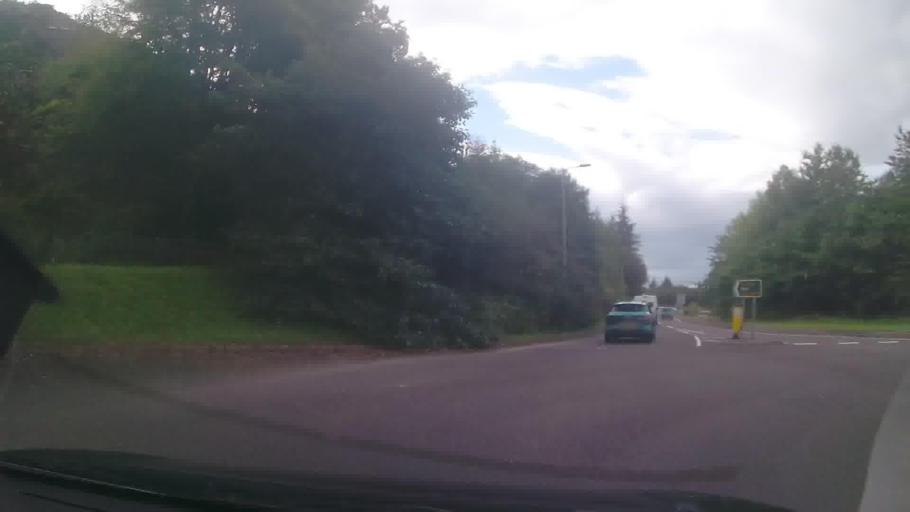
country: GB
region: Scotland
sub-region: Argyll and Bute
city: Oban
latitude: 56.5440
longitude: -5.2930
